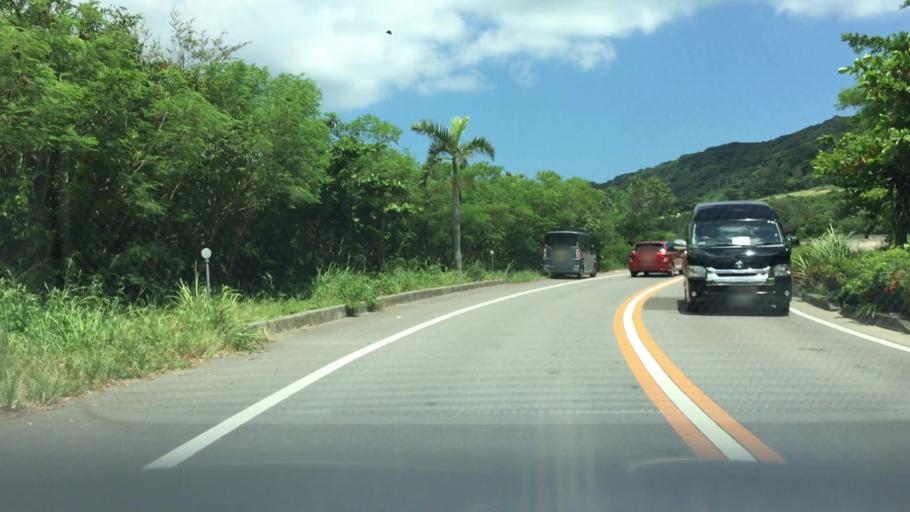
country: JP
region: Okinawa
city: Ishigaki
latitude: 24.4286
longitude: 124.1245
